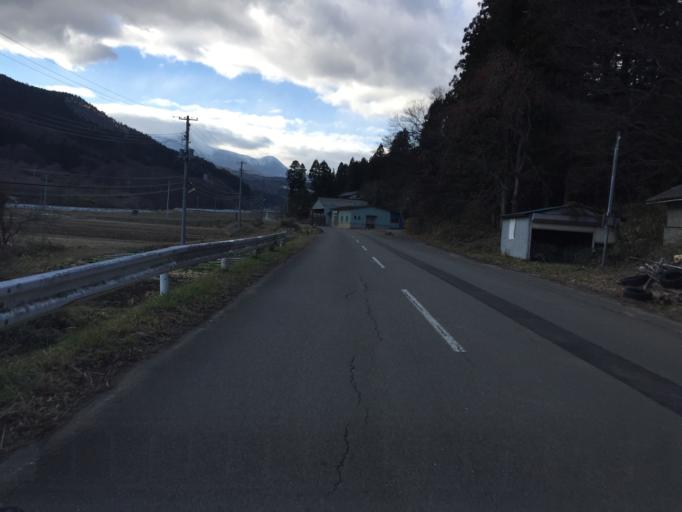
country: JP
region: Fukushima
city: Nihommatsu
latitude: 37.6720
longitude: 140.4009
